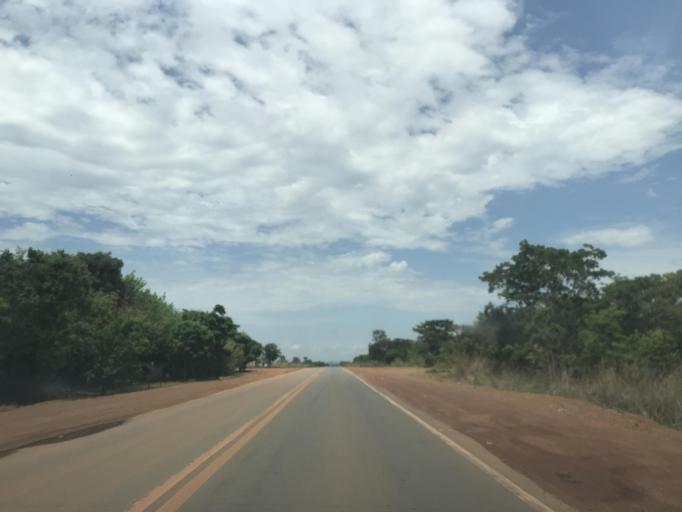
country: BR
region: Goias
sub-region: Luziania
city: Luziania
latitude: -16.3457
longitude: -48.0205
